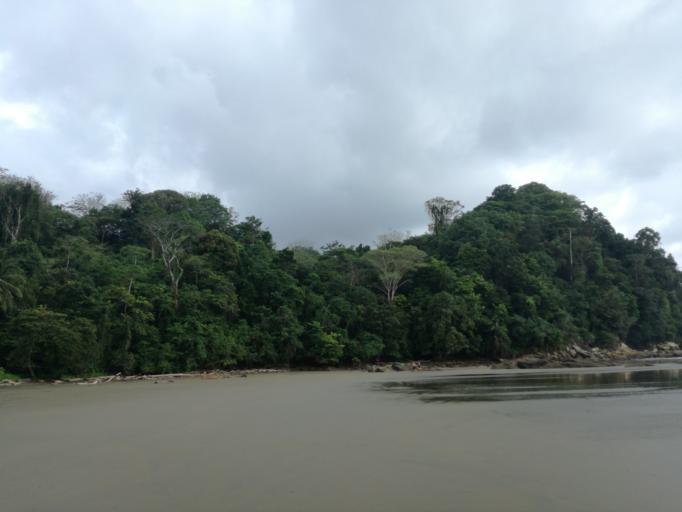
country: CR
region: San Jose
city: Mercedes
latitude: 9.1457
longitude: -83.7286
